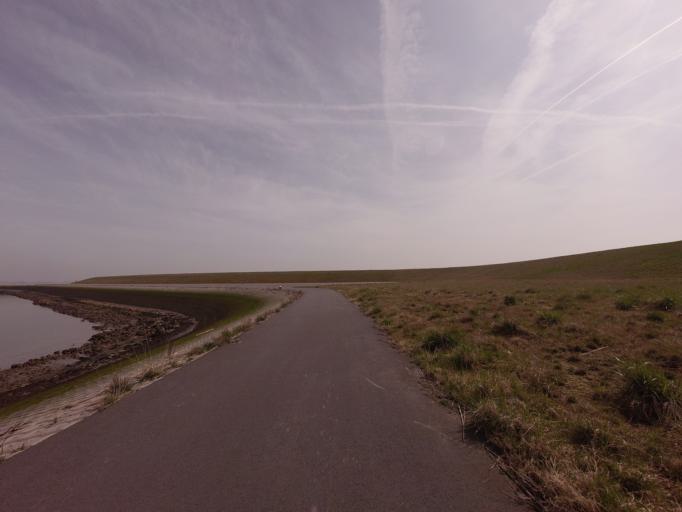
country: NL
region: Zeeland
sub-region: Gemeente Reimerswaal
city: Yerseke
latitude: 51.3970
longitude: 4.0178
